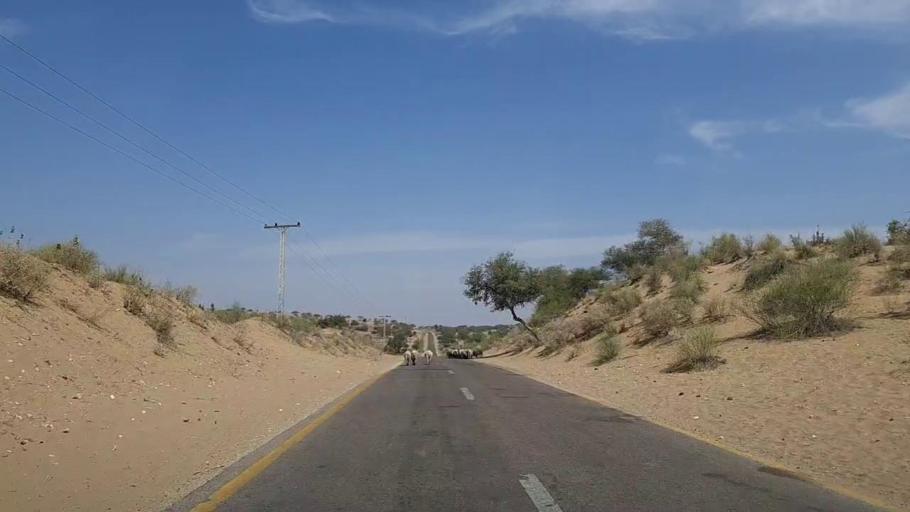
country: PK
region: Sindh
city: Mithi
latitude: 24.8345
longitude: 69.8322
